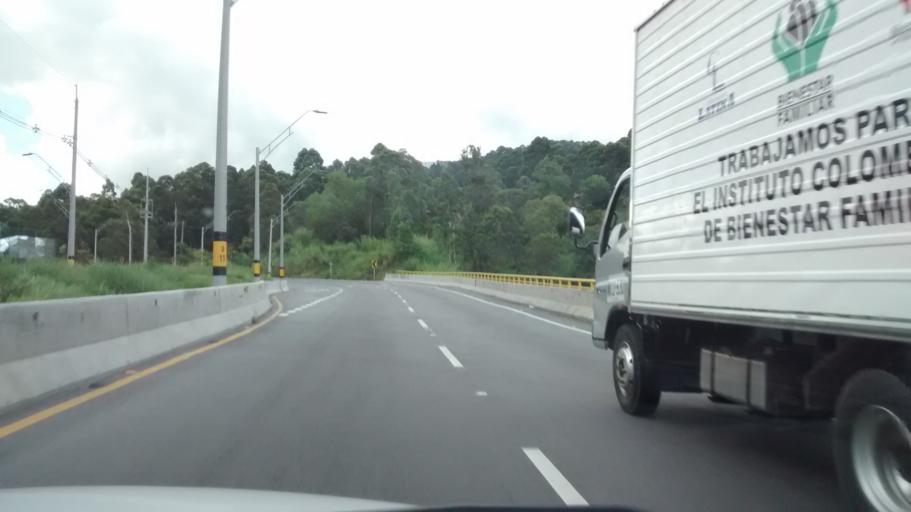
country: CO
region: Antioquia
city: Medellin
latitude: 6.2740
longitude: -75.6213
